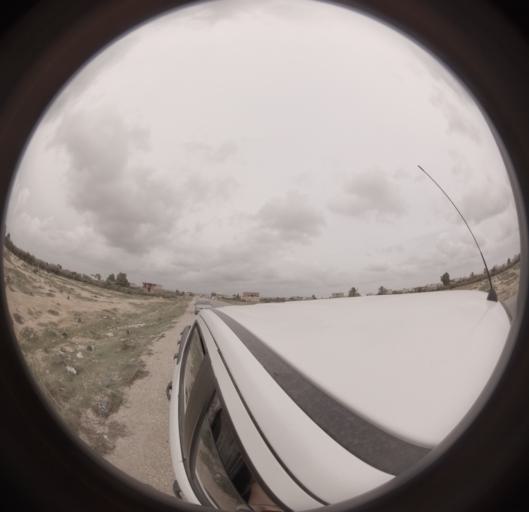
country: TN
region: Al Munastir
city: Jammal
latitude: 35.6153
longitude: 10.7406
